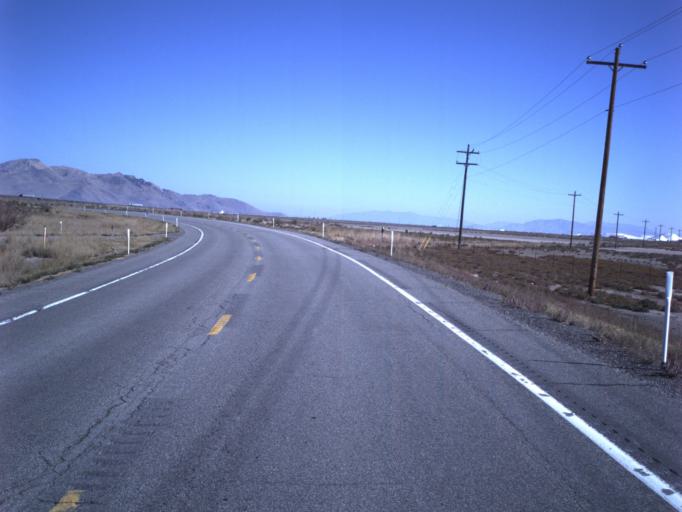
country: US
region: Utah
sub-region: Tooele County
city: Grantsville
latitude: 40.6965
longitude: -112.5305
